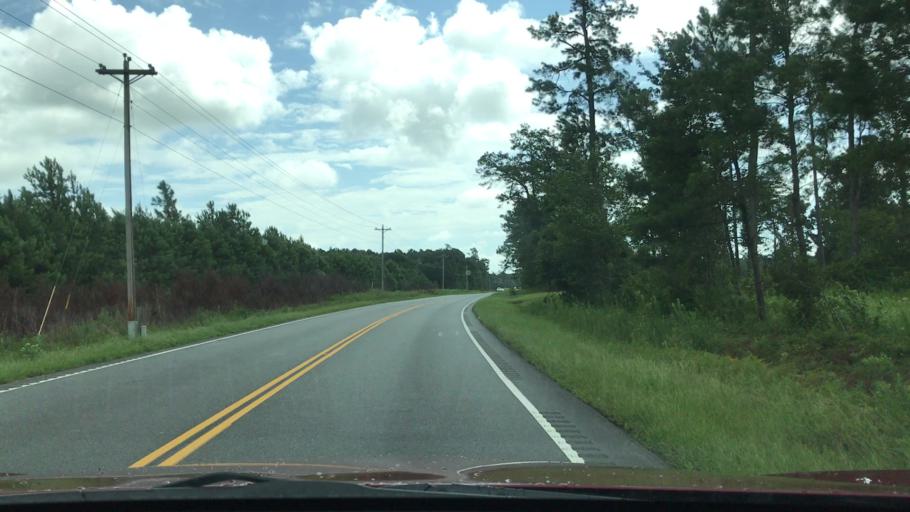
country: US
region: South Carolina
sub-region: Horry County
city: North Myrtle Beach
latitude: 33.9237
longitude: -78.7959
